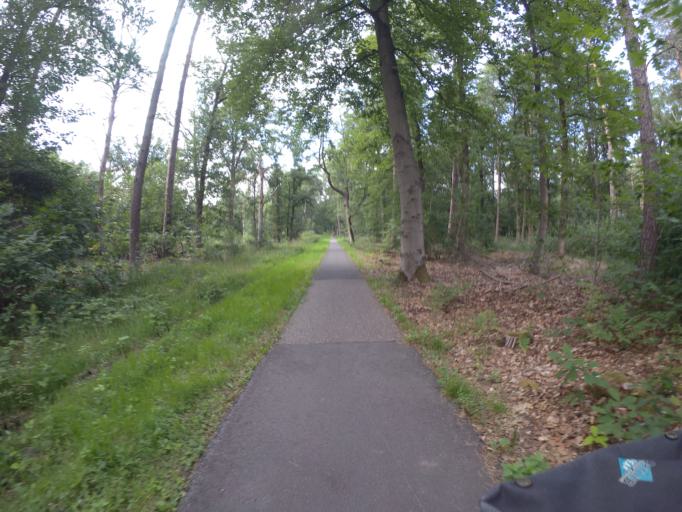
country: NL
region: North Brabant
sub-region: Gemeente Heeze-Leende
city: Heeze
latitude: 51.3881
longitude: 5.5276
